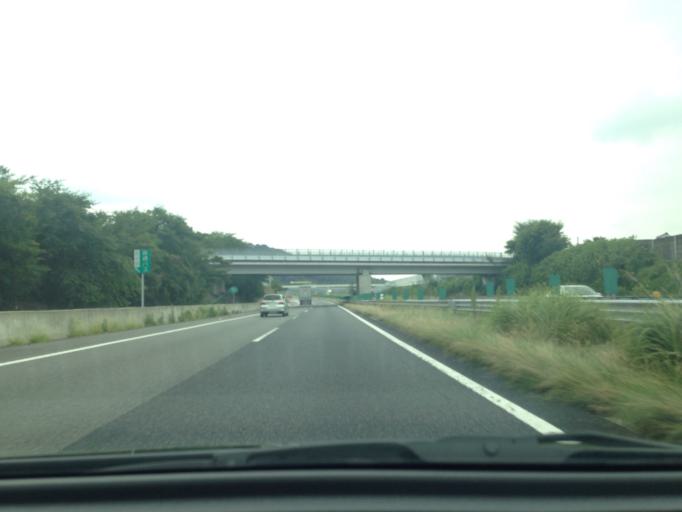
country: JP
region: Aichi
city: Shinshiro
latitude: 34.8195
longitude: 137.5502
